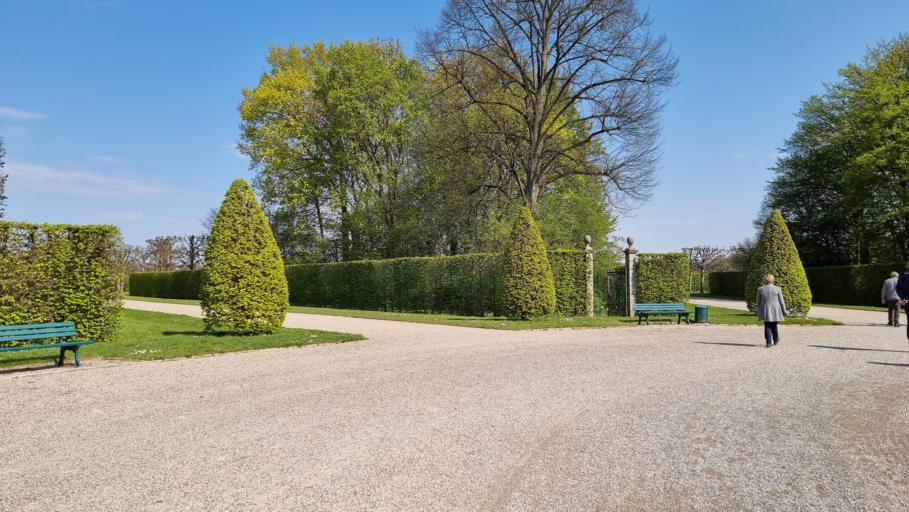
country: DE
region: Lower Saxony
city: Hannover
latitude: 52.3868
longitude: 9.6975
